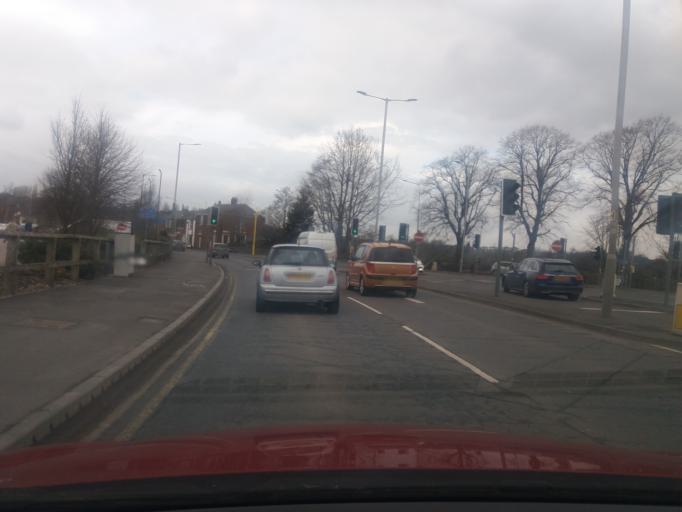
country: GB
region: England
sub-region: Lancashire
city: Preston
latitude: 53.7498
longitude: -2.6754
